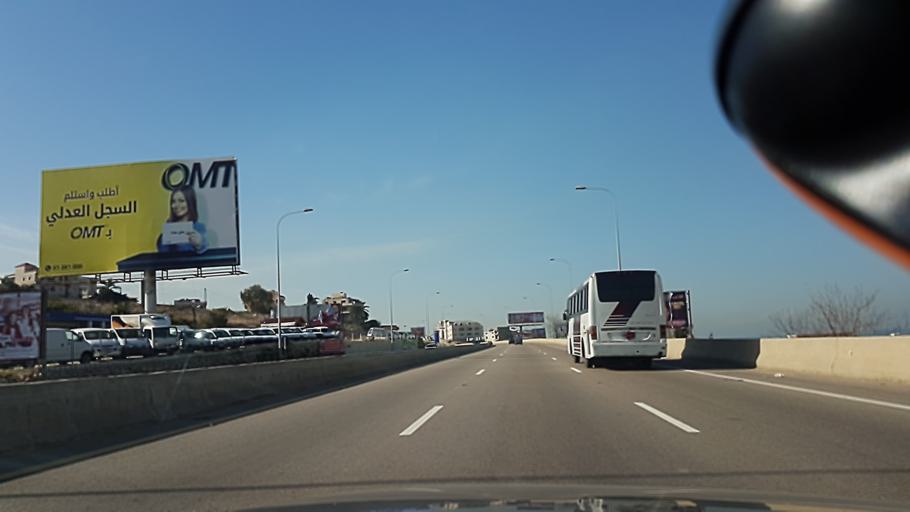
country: LB
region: Liban-Sud
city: Sidon
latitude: 33.6064
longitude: 35.3971
